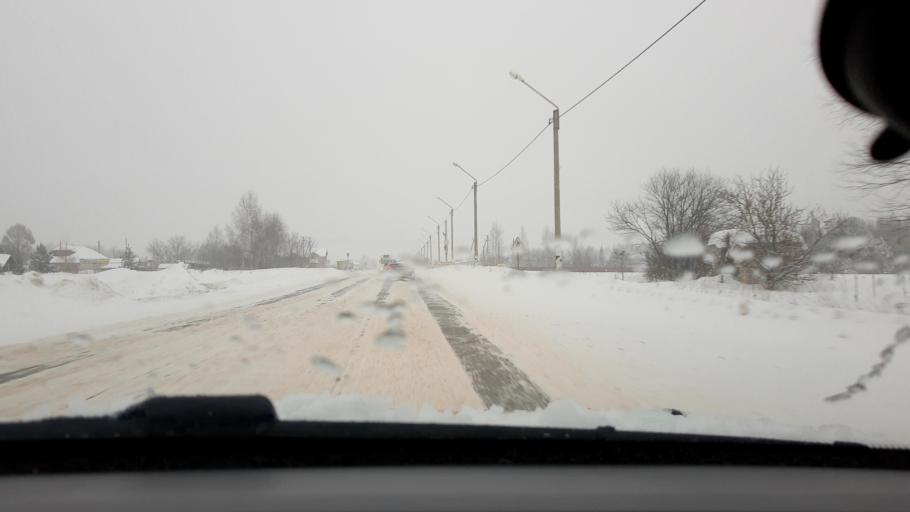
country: RU
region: Nizjnij Novgorod
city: Purekh
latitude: 56.6627
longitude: 43.1003
